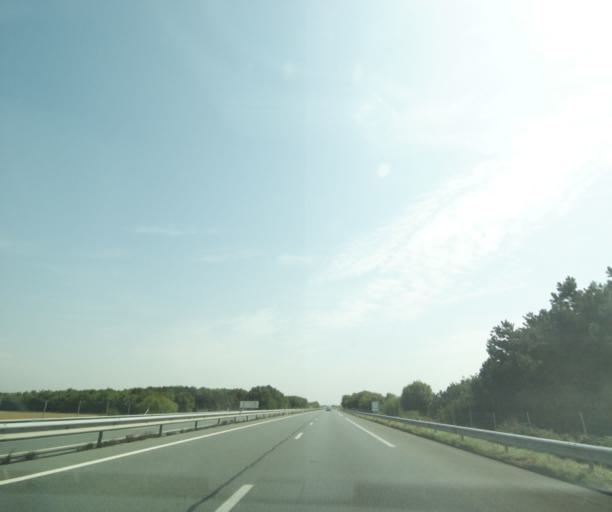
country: FR
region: Pays de la Loire
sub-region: Departement de la Vendee
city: Nalliers
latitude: 46.5147
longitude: -1.0293
